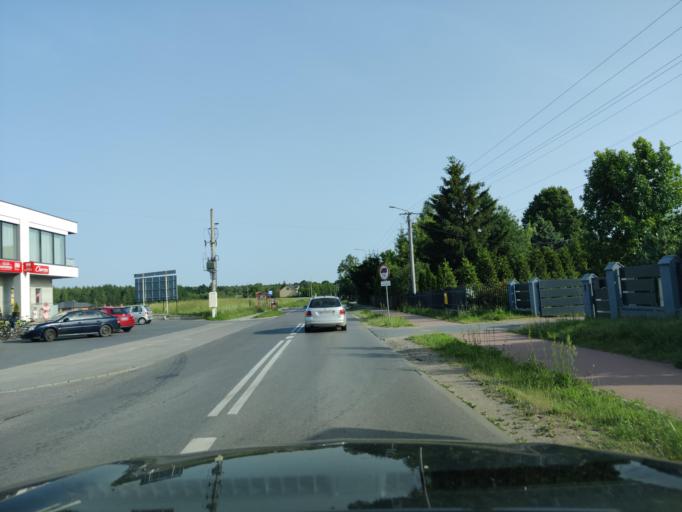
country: PL
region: Masovian Voivodeship
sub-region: Powiat wyszkowski
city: Wyszkow
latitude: 52.6464
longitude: 21.4509
